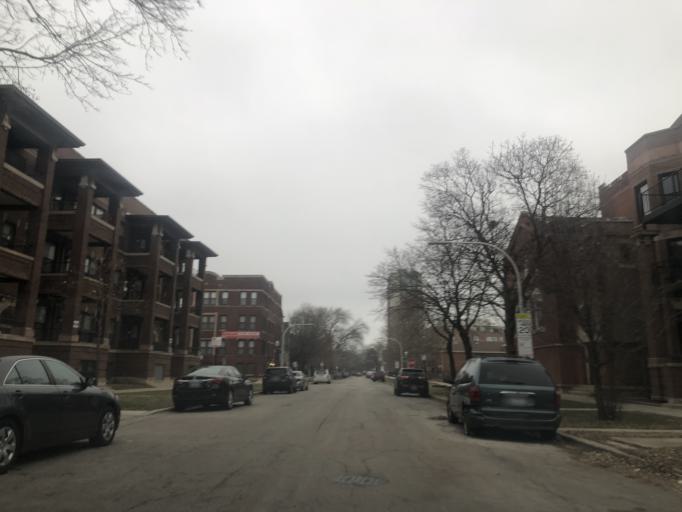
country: US
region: Illinois
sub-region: Cook County
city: Chicago
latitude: 41.7817
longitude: -87.5978
